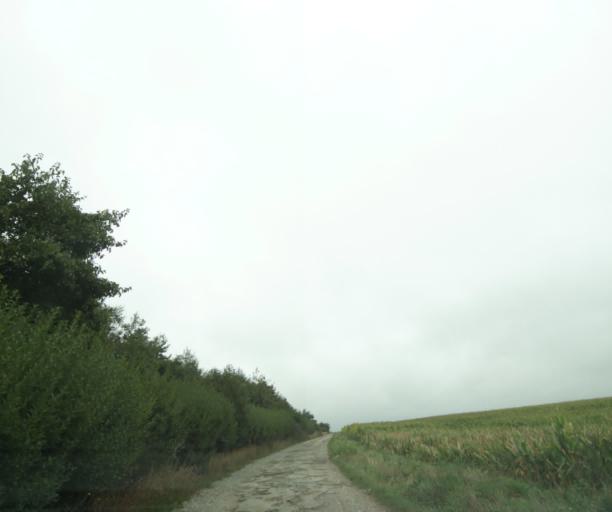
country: FR
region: Nord-Pas-de-Calais
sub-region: Departement du Pas-de-Calais
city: Etaples
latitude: 50.5210
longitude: 1.6806
